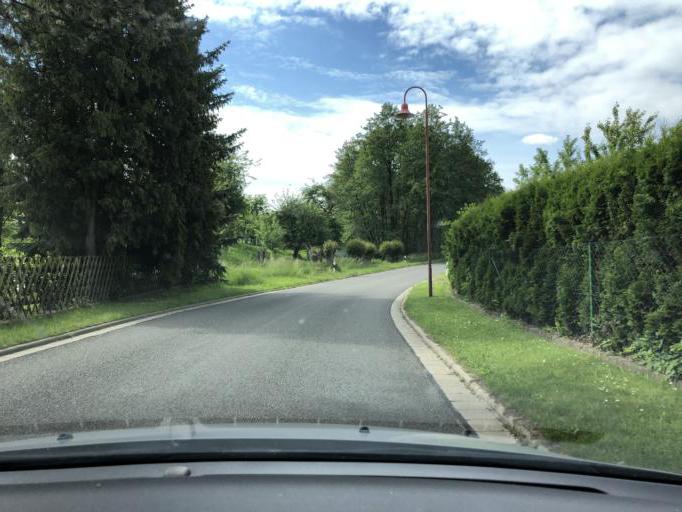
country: DE
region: Saxony
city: Nerchau
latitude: 51.2159
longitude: 12.8111
